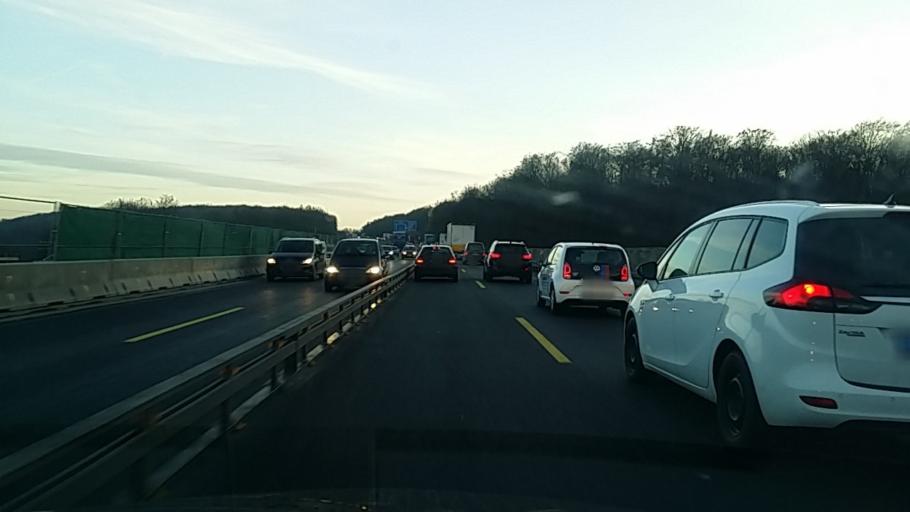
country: DE
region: Bavaria
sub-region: Regierungsbezirk Unterfranken
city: Estenfeld
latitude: 49.8591
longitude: 9.9949
